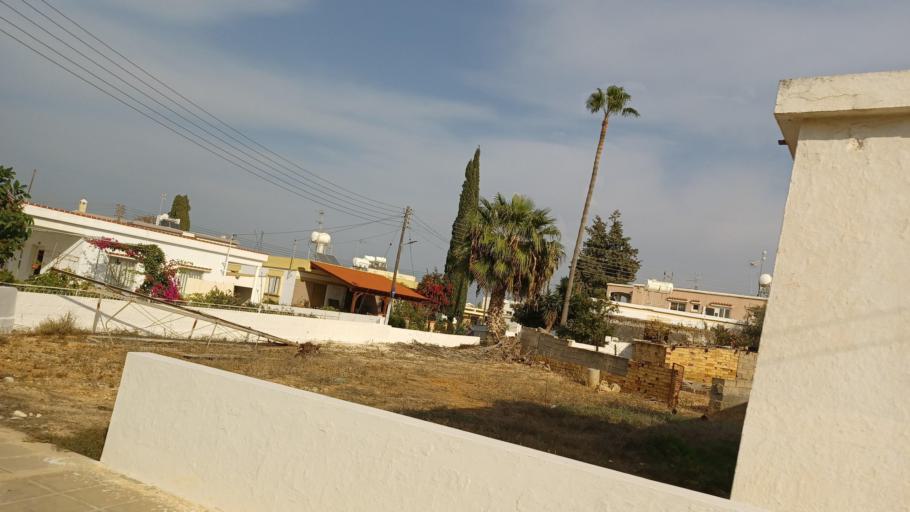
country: CY
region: Ammochostos
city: Frenaros
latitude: 35.0432
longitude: 33.9216
